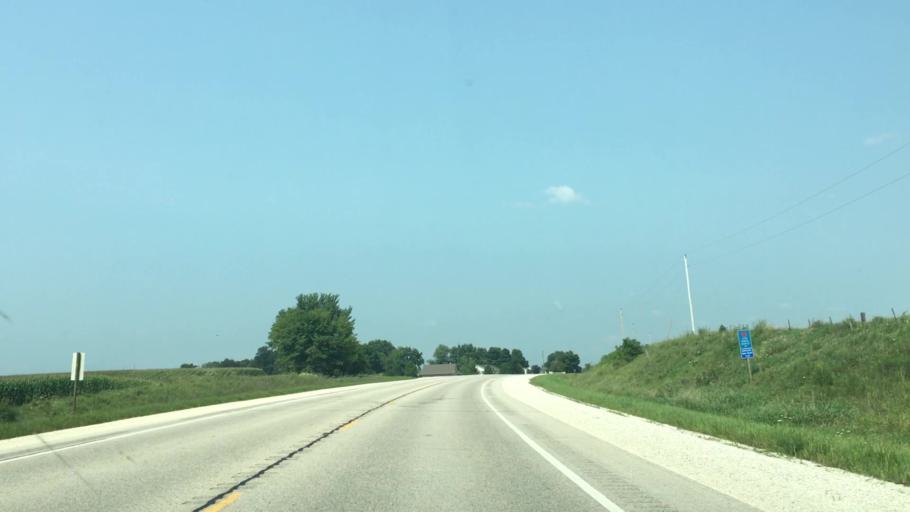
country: US
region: Iowa
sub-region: Winneshiek County
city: Decorah
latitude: 43.2603
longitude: -91.8380
